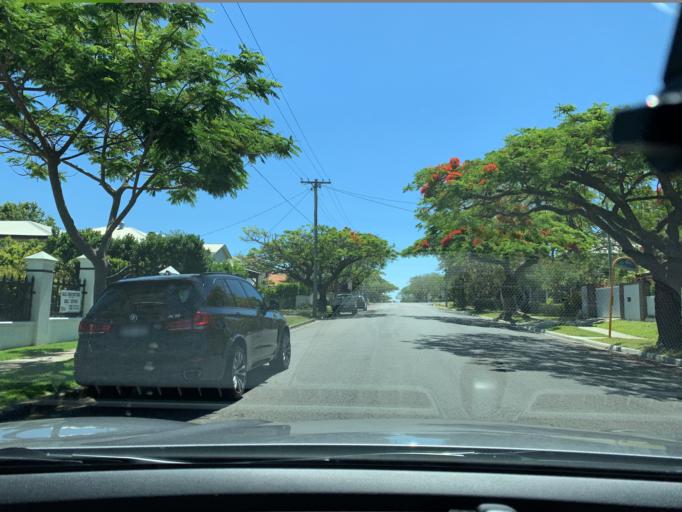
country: AU
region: Queensland
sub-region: Brisbane
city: Ascot
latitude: -27.4227
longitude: 153.0690
